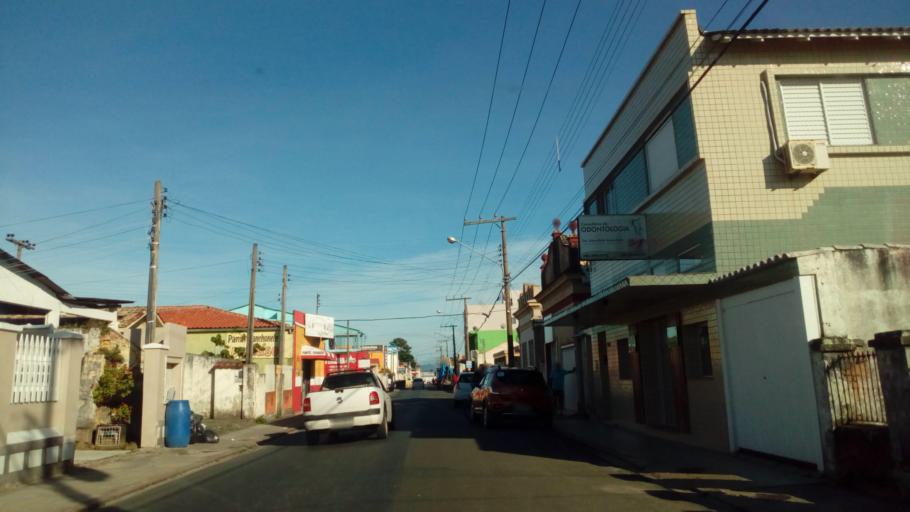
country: BR
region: Santa Catarina
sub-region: Laguna
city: Laguna
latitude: -28.4919
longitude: -48.7822
